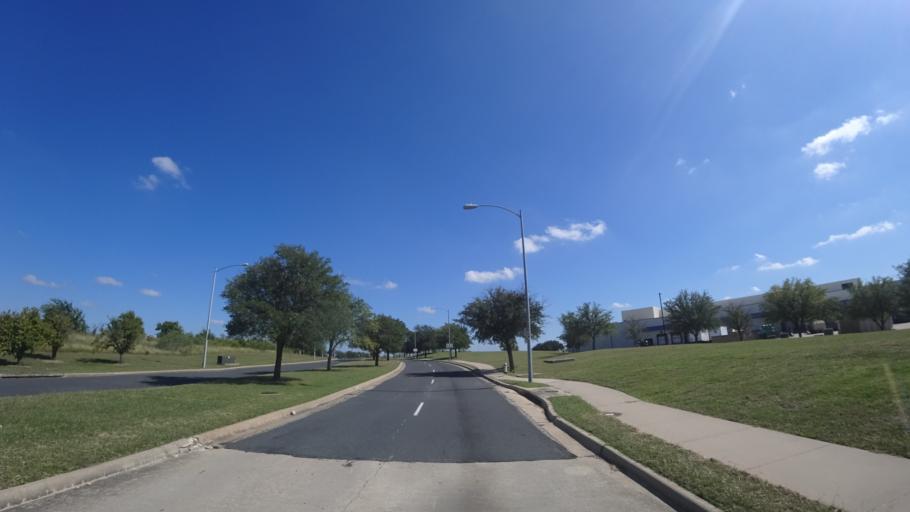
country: US
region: Texas
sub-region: Travis County
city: Manor
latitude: 30.3428
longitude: -97.6152
